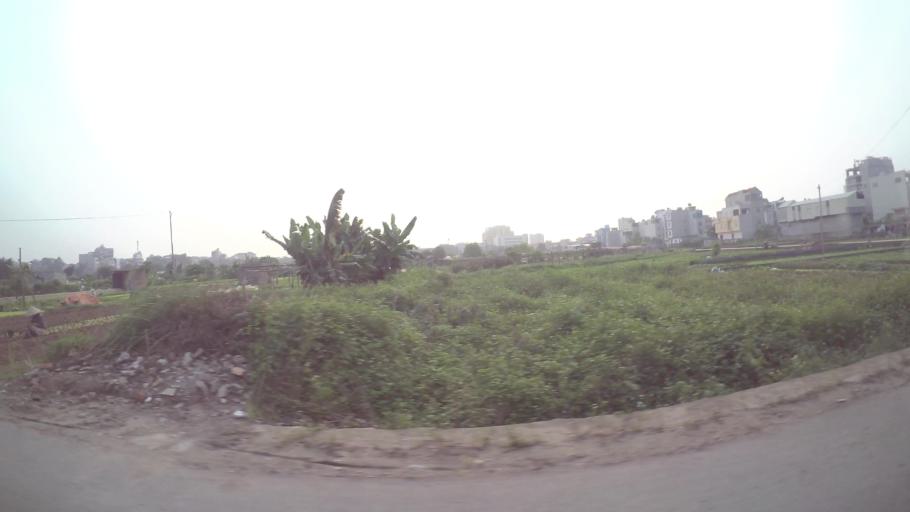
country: VN
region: Ha Noi
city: Thuong Tin
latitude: 20.8696
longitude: 105.8705
